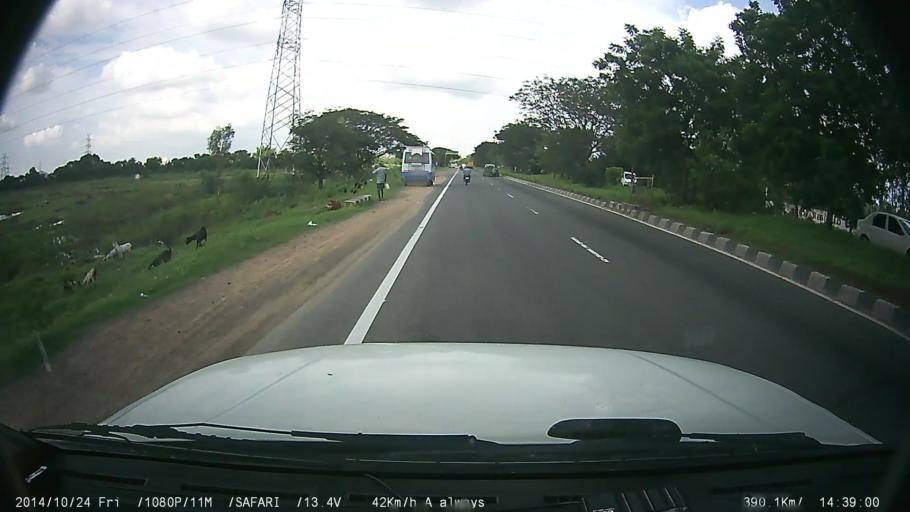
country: IN
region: Tamil Nadu
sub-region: Kancheepuram
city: Singapperumalkovil
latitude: 12.7468
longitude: 79.9952
